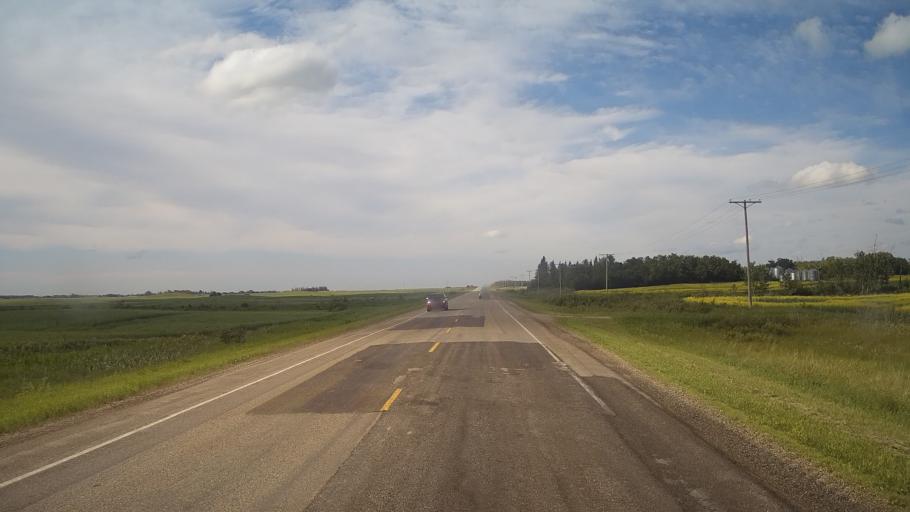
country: CA
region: Saskatchewan
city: Foam Lake
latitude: 51.6028
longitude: -103.8458
